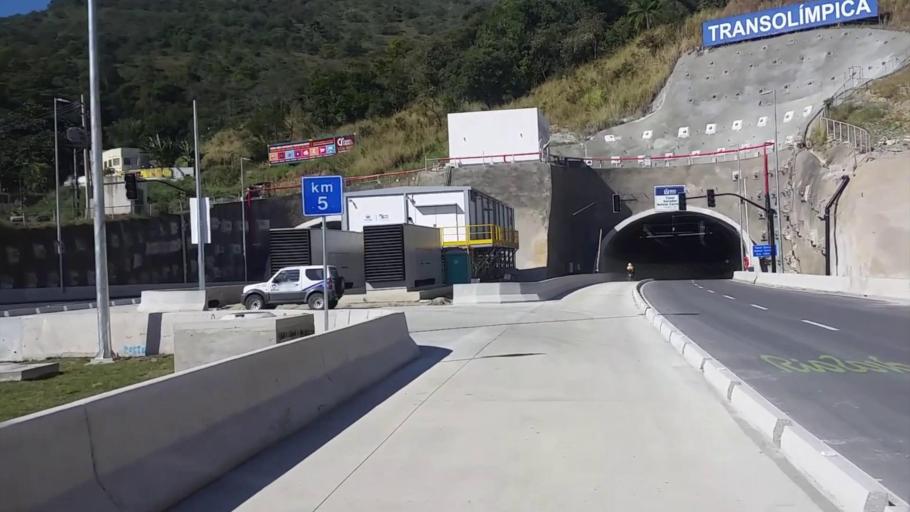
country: BR
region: Rio de Janeiro
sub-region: Nilopolis
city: Nilopolis
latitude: -22.8982
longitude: -43.3980
